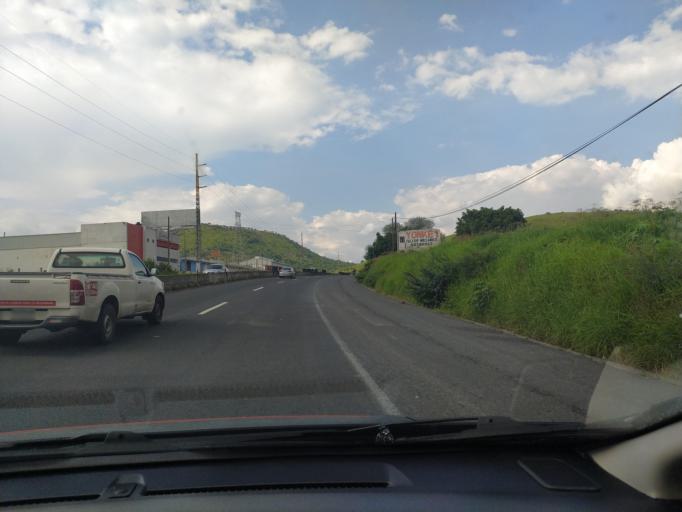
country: MX
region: Jalisco
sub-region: Acatlan de Juarez
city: Villa de los Ninos
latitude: 20.4311
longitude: -103.5807
